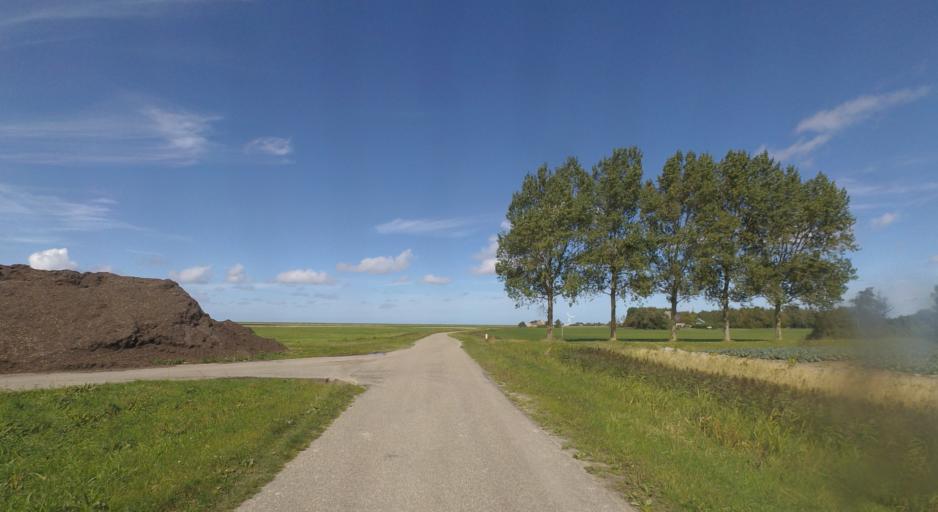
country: NL
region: Friesland
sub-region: Gemeente Dongeradeel
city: Holwerd
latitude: 53.3609
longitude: 5.8969
